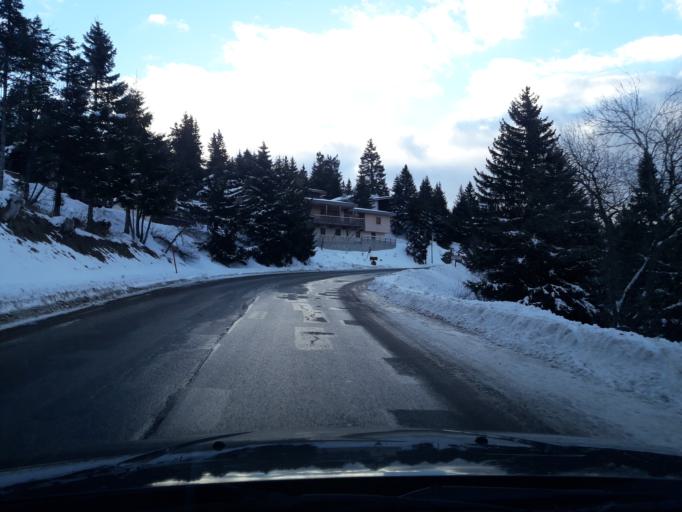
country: FR
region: Rhone-Alpes
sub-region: Departement de l'Isere
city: Vaulnaveys-le-Bas
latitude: 45.1155
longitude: 5.8735
